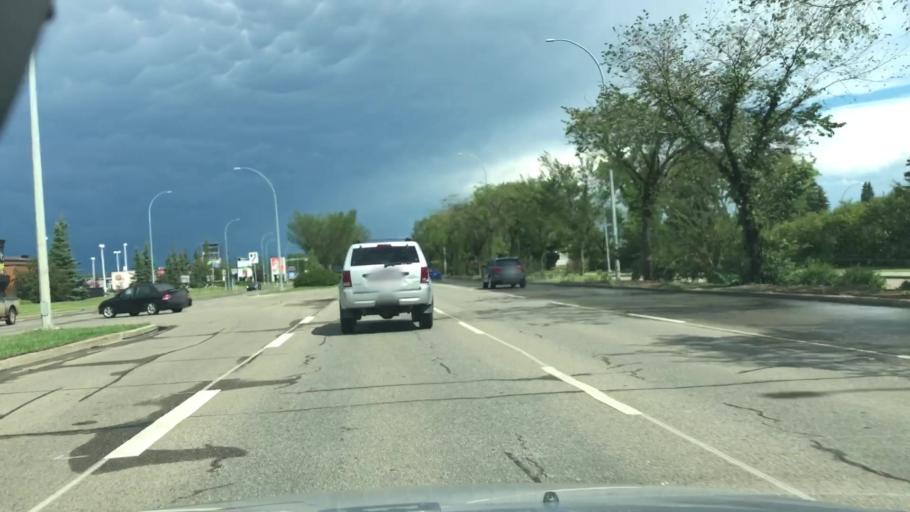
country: CA
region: Alberta
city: St. Albert
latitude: 53.5994
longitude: -113.5568
